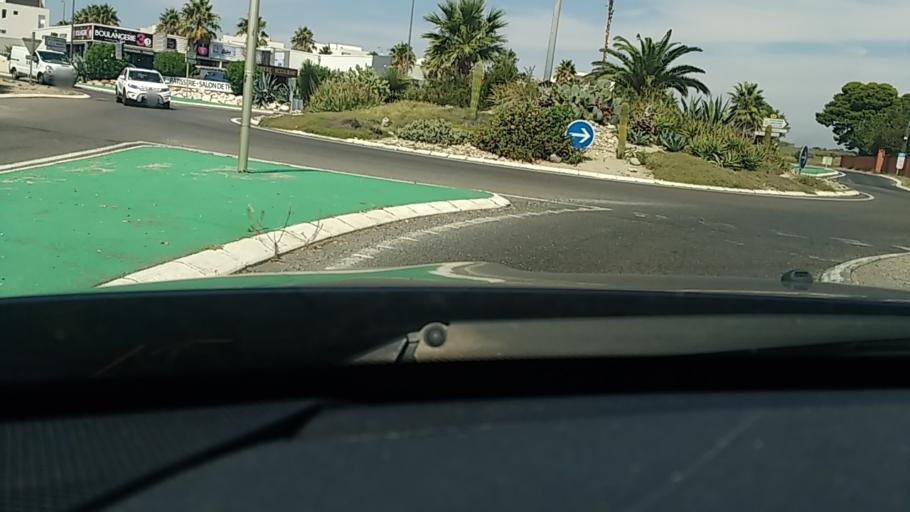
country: FR
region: Languedoc-Roussillon
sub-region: Departement des Pyrenees-Orientales
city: Villeneuve-de-la-Raho
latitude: 42.6370
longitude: 2.9231
